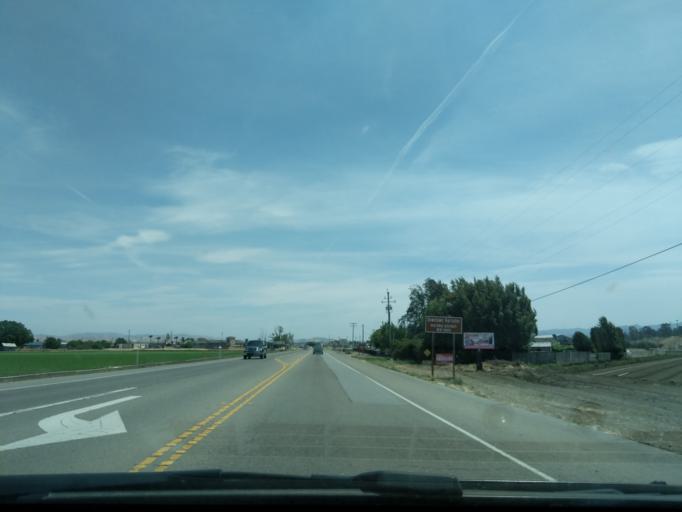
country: US
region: California
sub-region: San Benito County
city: Hollister
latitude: 36.8692
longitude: -121.4062
